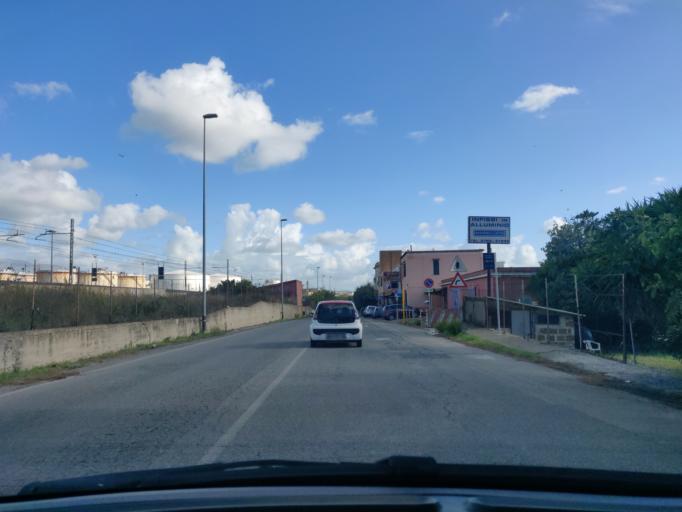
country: IT
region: Latium
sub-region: Citta metropolitana di Roma Capitale
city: Aurelia
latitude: 42.1130
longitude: 11.7751
